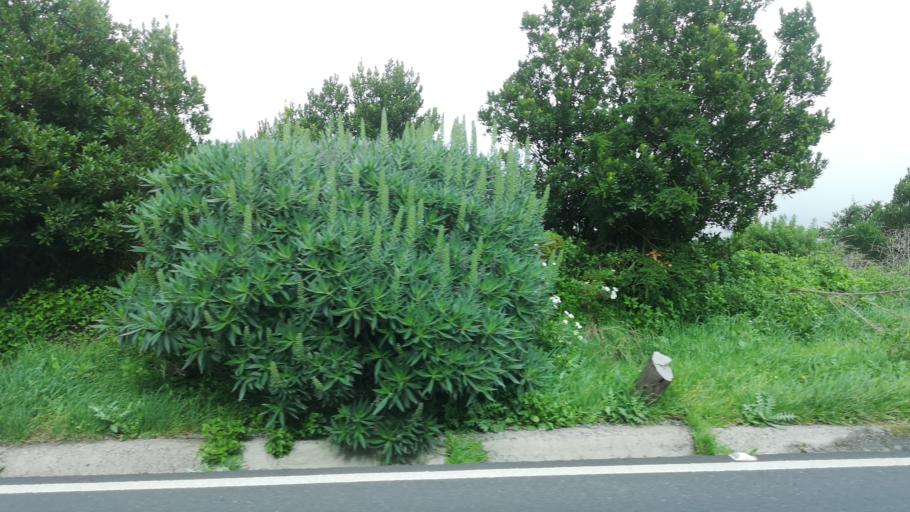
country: ES
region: Canary Islands
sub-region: Provincia de Santa Cruz de Tenerife
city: Alajero
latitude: 28.1061
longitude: -17.2125
